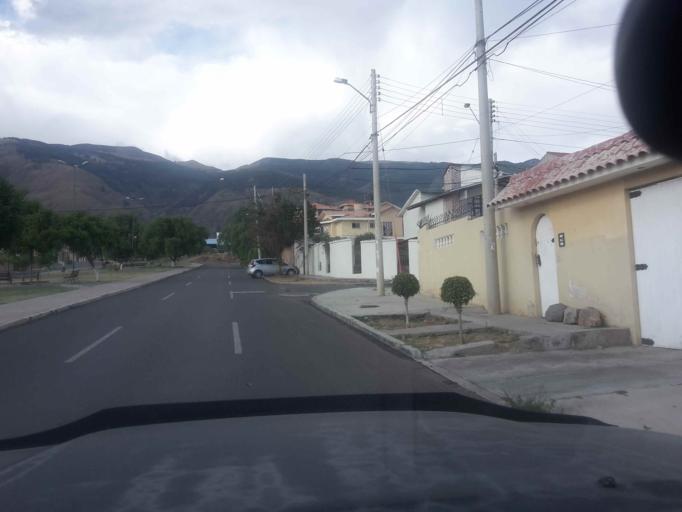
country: BO
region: Cochabamba
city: Cochabamba
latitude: -17.3579
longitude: -66.1691
